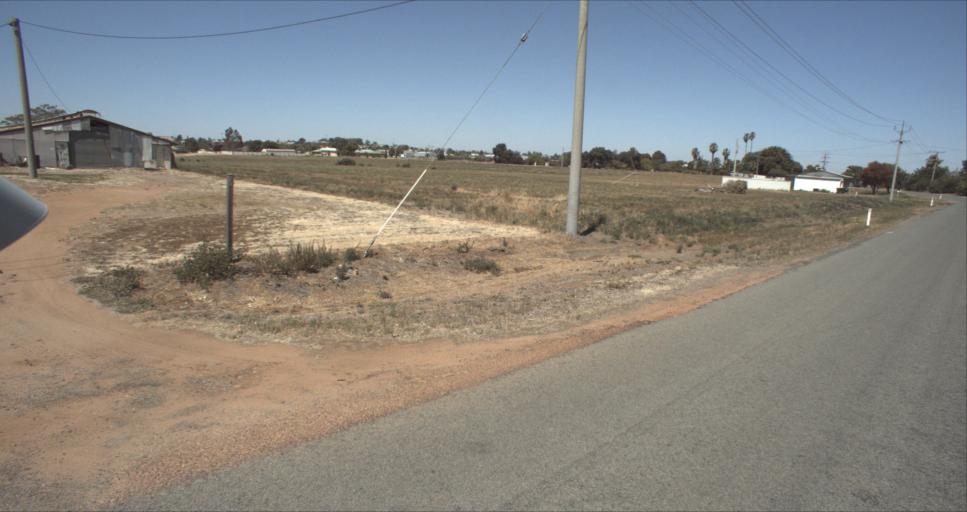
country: AU
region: New South Wales
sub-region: Leeton
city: Leeton
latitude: -34.5414
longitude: 146.3949
